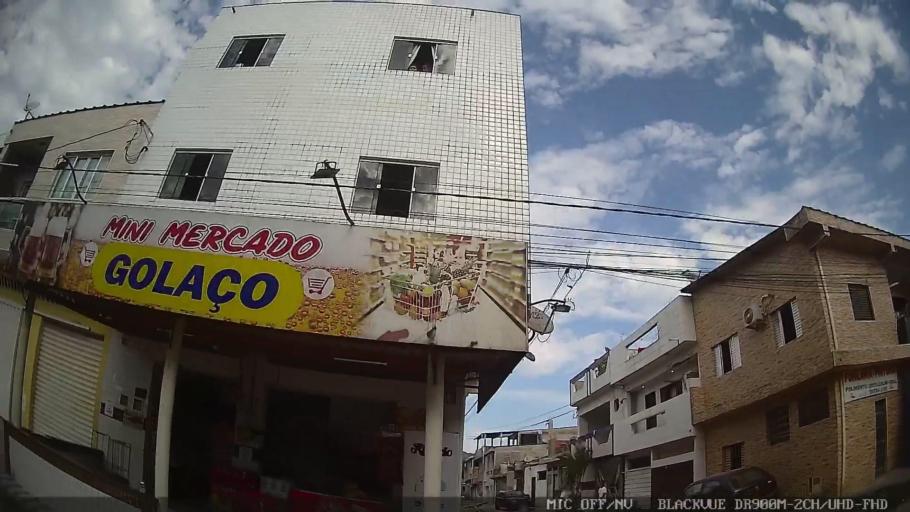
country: BR
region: Sao Paulo
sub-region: Guaruja
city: Guaruja
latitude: -23.9599
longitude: -46.2495
